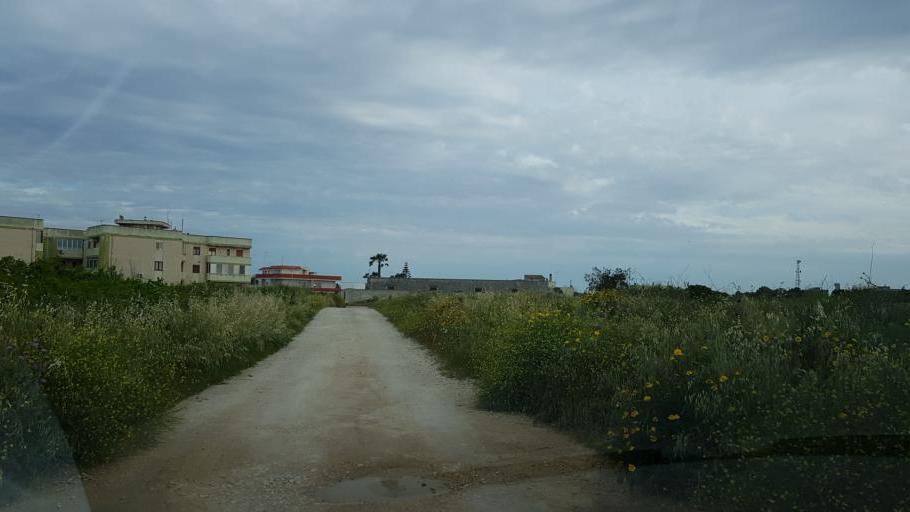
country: IT
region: Apulia
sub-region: Provincia di Brindisi
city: Materdomini
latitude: 40.6565
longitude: 17.9537
